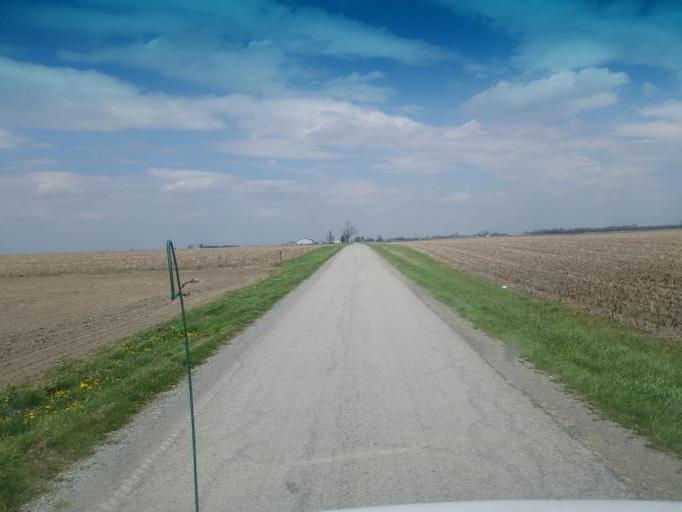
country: US
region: Ohio
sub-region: Wyandot County
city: Upper Sandusky
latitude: 40.7919
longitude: -83.3040
